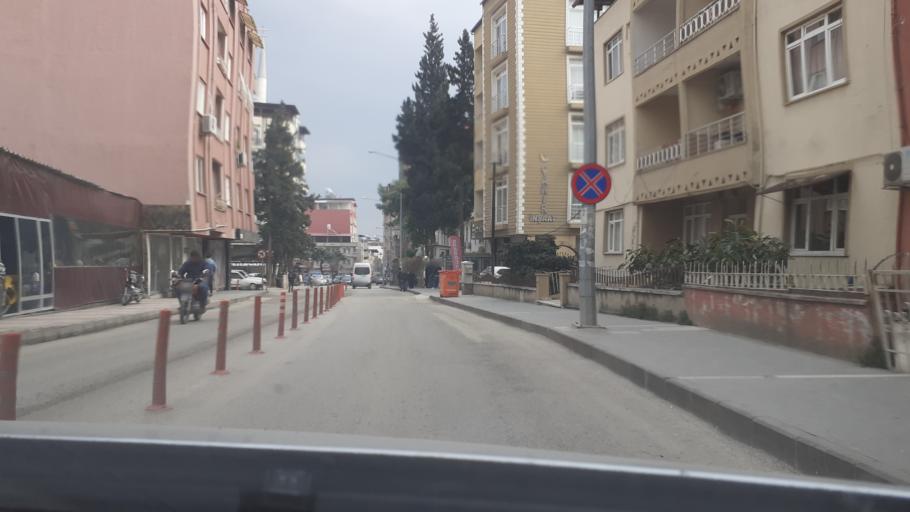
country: TR
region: Hatay
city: Kirikhan
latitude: 36.4981
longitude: 36.3529
